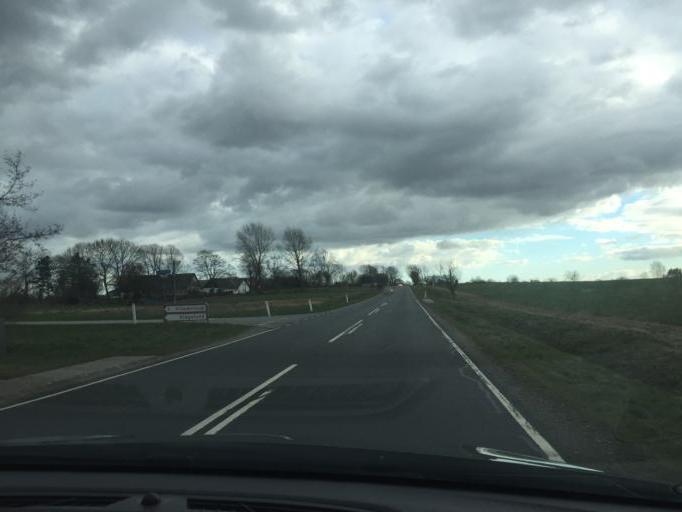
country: DK
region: South Denmark
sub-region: Kerteminde Kommune
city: Langeskov
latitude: 55.2891
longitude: 10.6090
